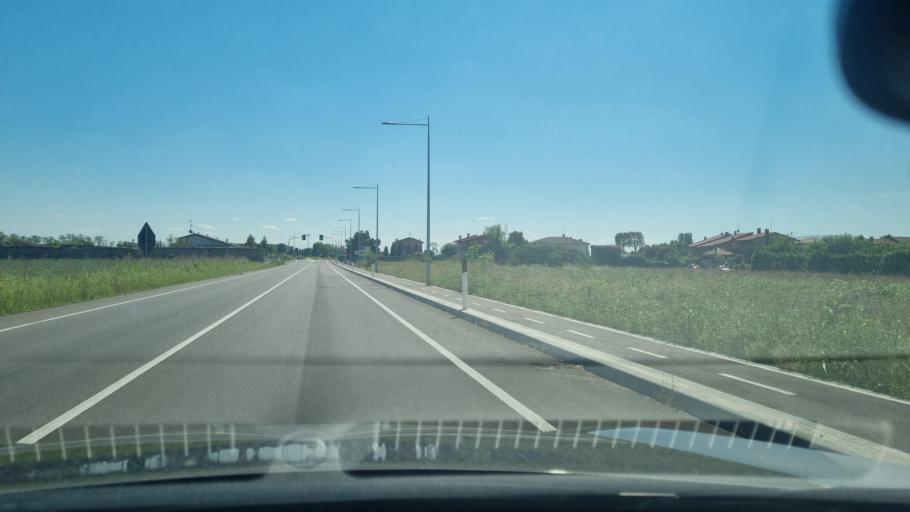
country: IT
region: Lombardy
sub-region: Provincia di Bergamo
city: Ghisalba
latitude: 45.5969
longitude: 9.7705
